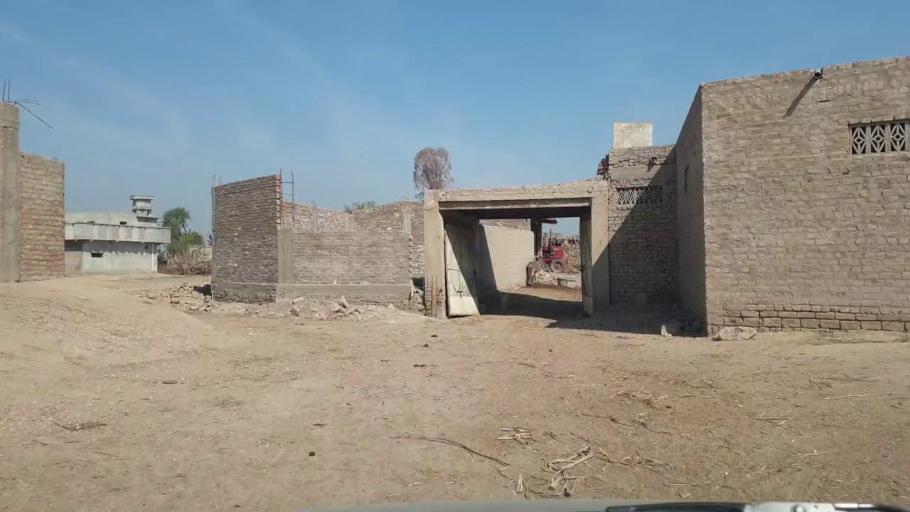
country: PK
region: Sindh
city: Tando Allahyar
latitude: 25.3892
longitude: 68.7829
